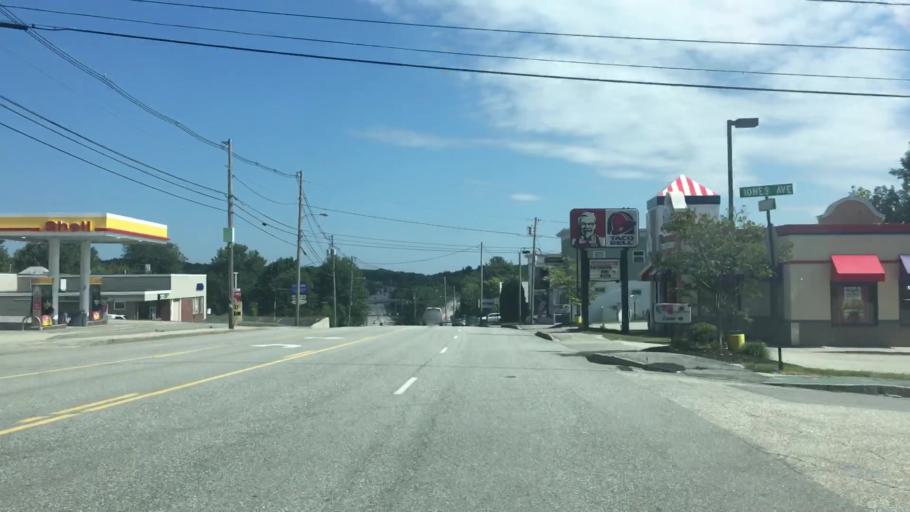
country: US
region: Maine
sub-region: Androscoggin County
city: Lewiston
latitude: 44.0777
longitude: -70.1892
